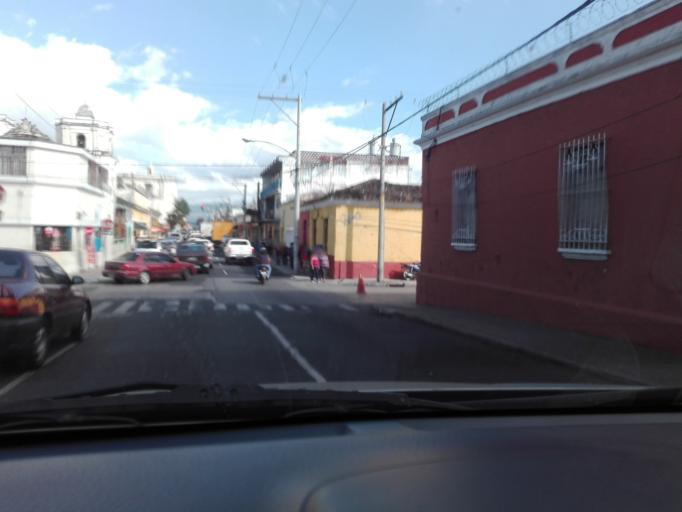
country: GT
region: Guatemala
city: Guatemala City
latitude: 14.6426
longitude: -90.5090
